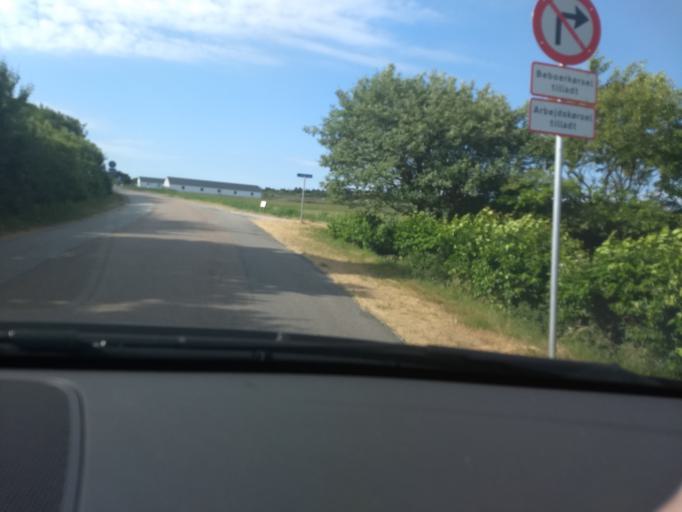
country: DE
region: Schleswig-Holstein
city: List
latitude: 55.0894
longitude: 8.5425
